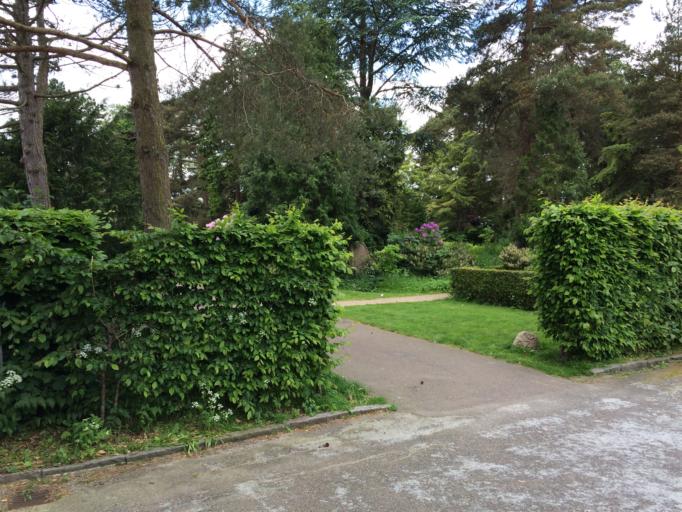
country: DK
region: Capital Region
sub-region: Gentofte Kommune
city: Charlottenlund
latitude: 55.7642
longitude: 12.5780
